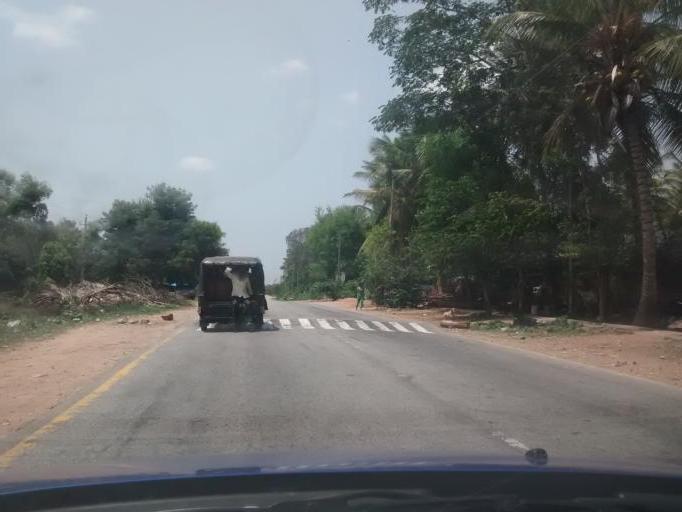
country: IN
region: Karnataka
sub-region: Mandya
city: Krishnarajpet
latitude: 12.5723
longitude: 76.3604
